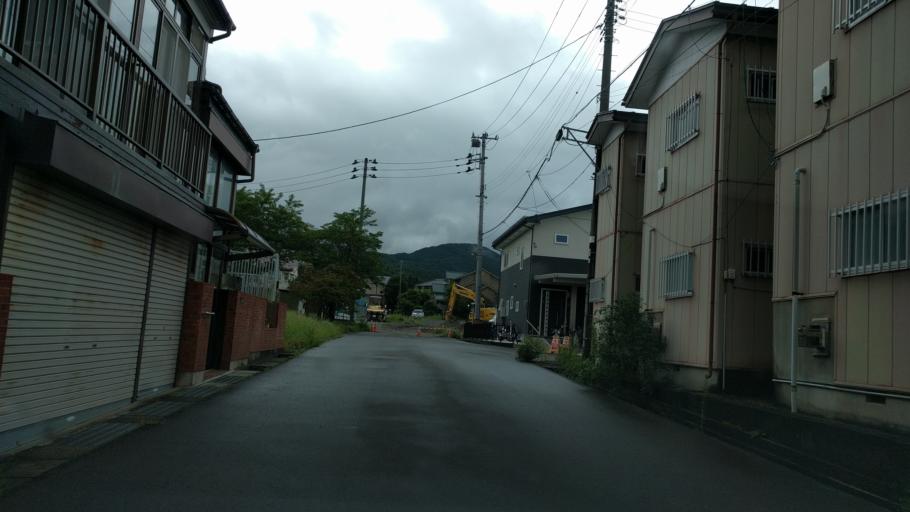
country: JP
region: Fukushima
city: Kitakata
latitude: 37.5091
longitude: 139.9497
